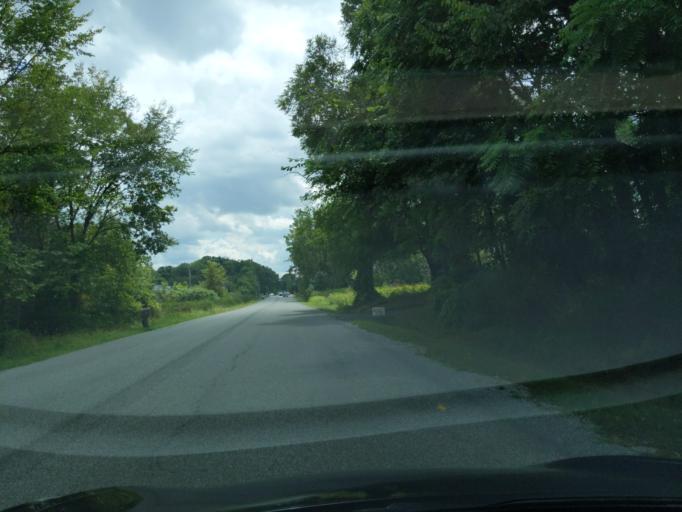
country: US
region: Michigan
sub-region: Eaton County
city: Dimondale
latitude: 42.6431
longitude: -84.5825
